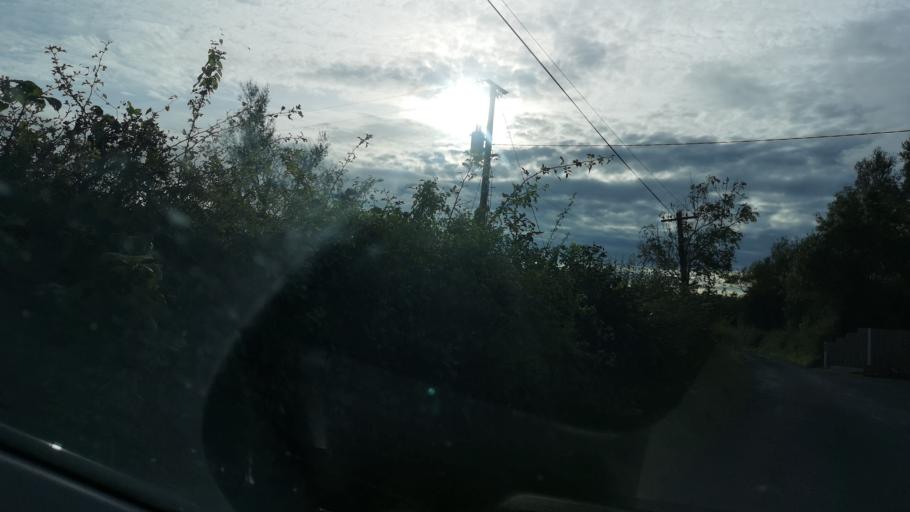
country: IE
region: Connaught
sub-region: County Galway
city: Ballinasloe
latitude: 53.3430
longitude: -8.2863
